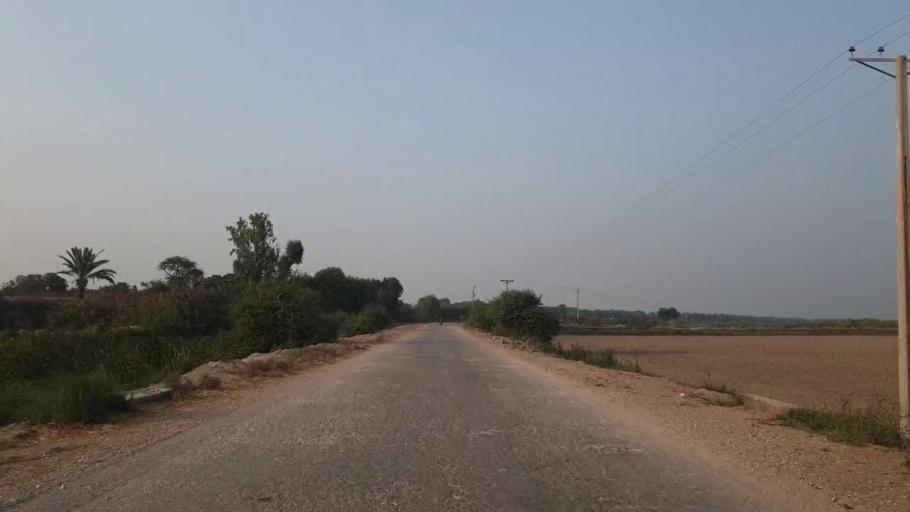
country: PK
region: Sindh
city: Tando Muhammad Khan
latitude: 25.1135
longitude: 68.4281
